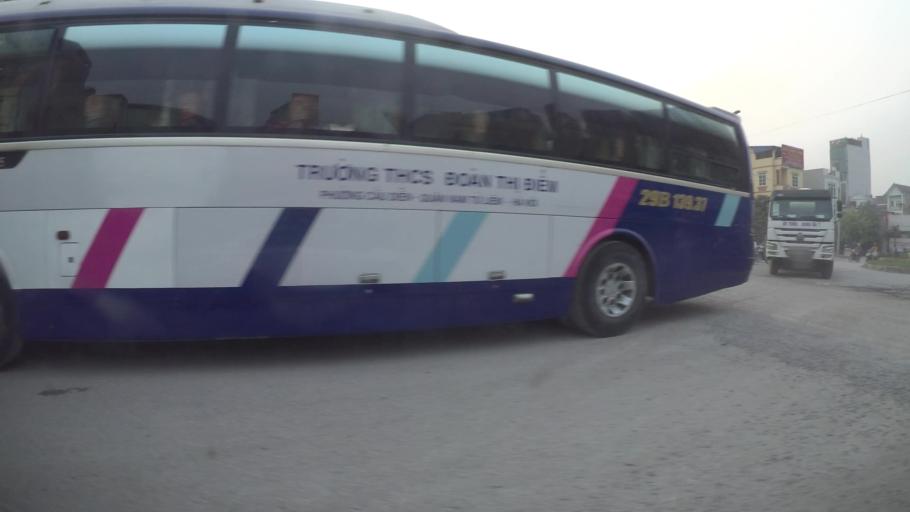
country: VN
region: Ha Noi
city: Cau Dien
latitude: 21.0079
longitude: 105.7203
